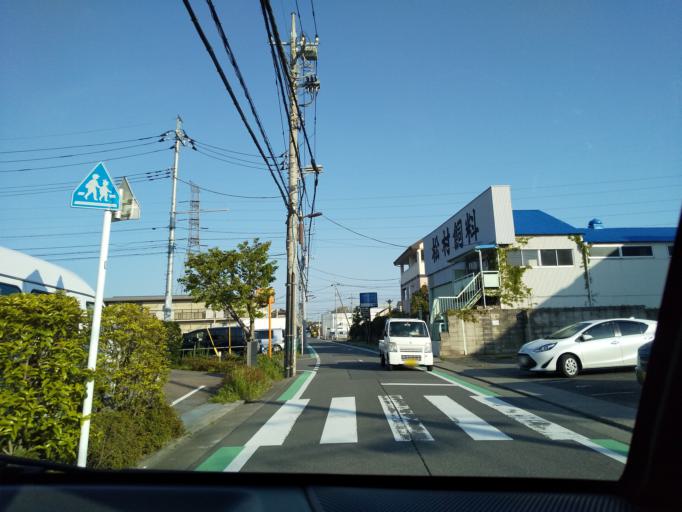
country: JP
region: Tokyo
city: Hino
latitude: 35.6681
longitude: 139.4408
